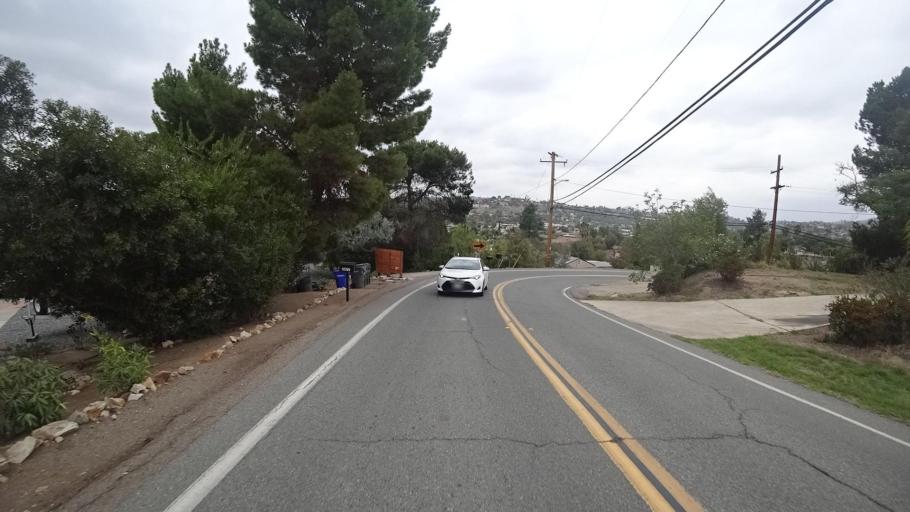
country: US
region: California
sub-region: San Diego County
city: Spring Valley
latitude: 32.7350
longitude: -117.0007
